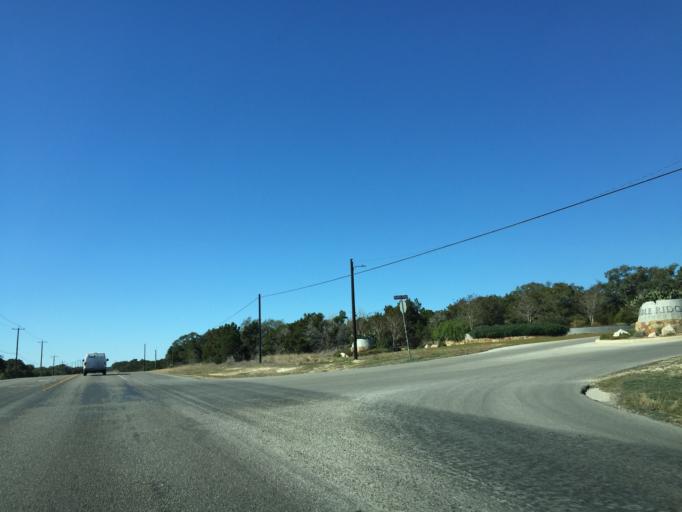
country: US
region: Texas
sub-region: Comal County
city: Garden Ridge
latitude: 29.6996
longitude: -98.3209
